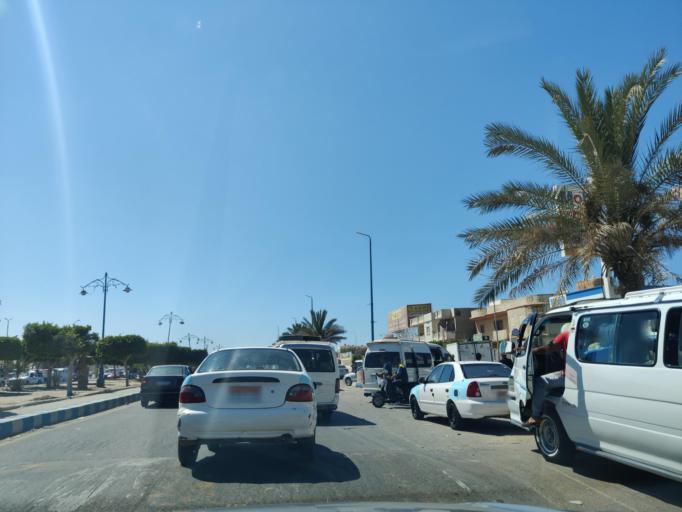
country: EG
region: Muhafazat Matruh
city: Mersa Matruh
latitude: 31.3387
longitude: 27.2513
